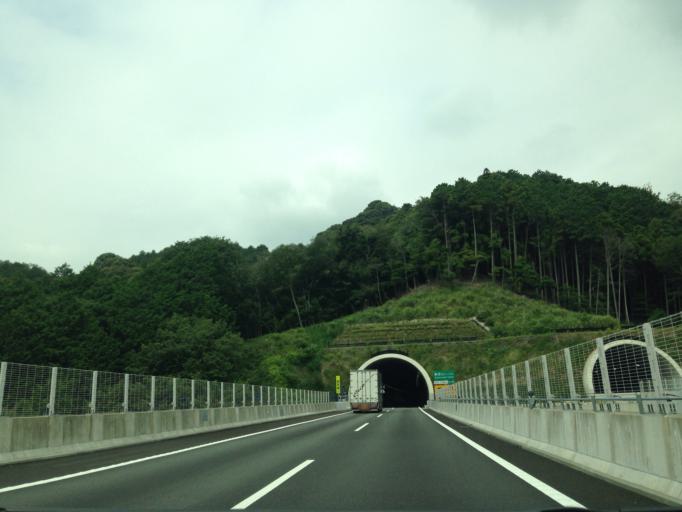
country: JP
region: Aichi
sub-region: Tokai-shi
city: Toyokawa
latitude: 34.8838
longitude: 137.3706
